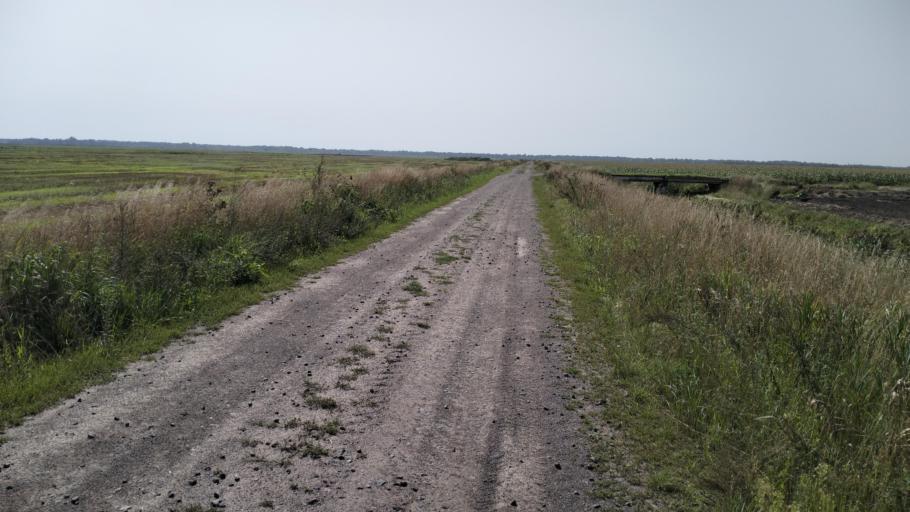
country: BY
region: Brest
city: Davyd-Haradok
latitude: 51.9937
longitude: 27.1647
